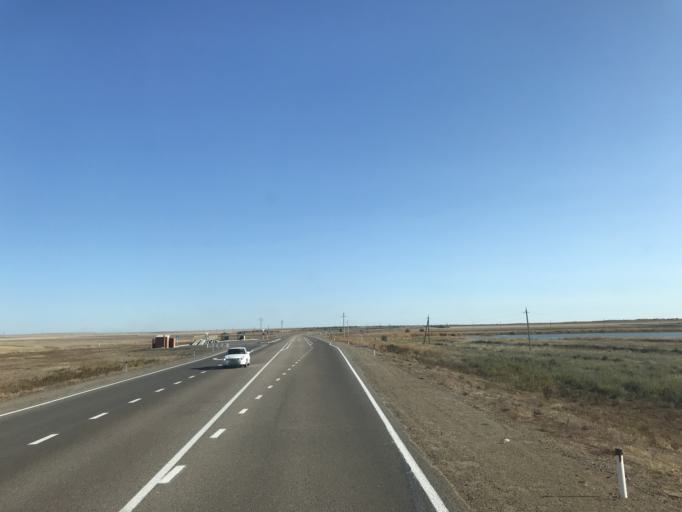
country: KZ
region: Pavlodar
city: Koktobe
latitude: 51.8837
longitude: 77.4164
